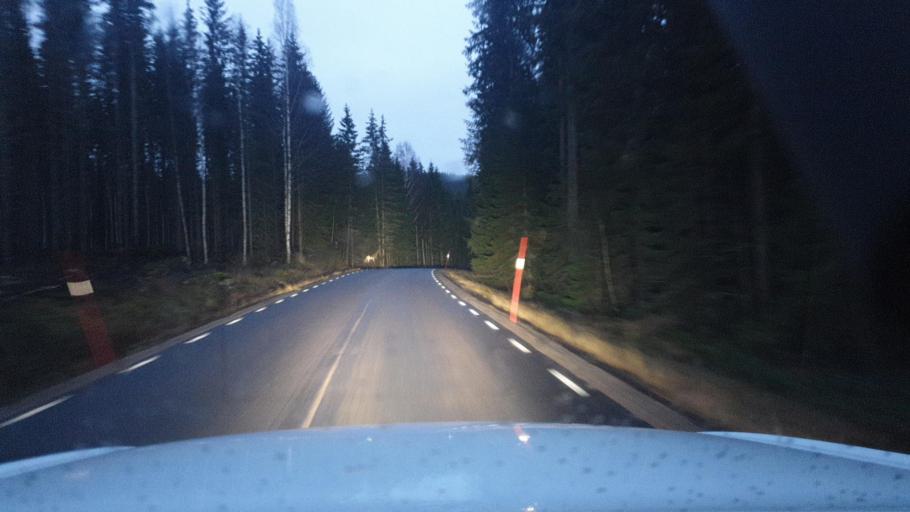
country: SE
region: Vaermland
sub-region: Torsby Kommun
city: Torsby
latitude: 60.0010
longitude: 12.7311
